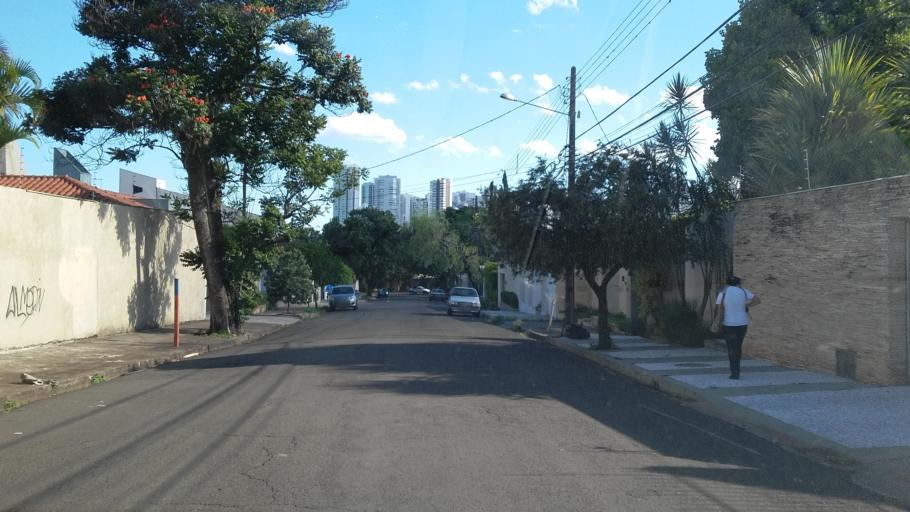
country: BR
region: Parana
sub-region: Londrina
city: Londrina
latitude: -23.3202
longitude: -51.1759
